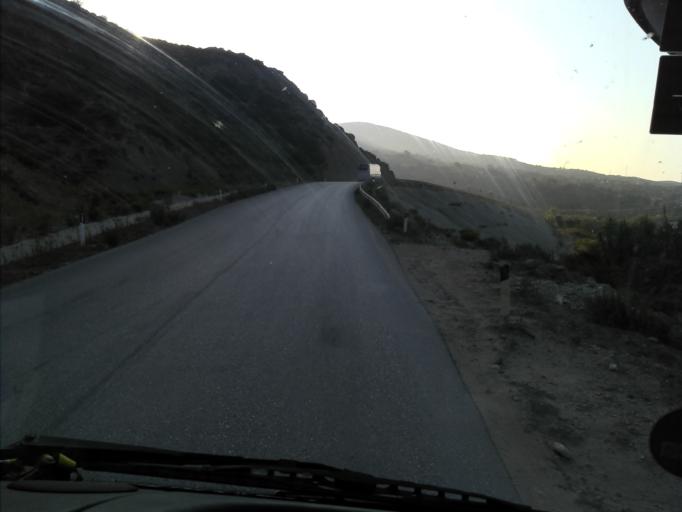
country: AL
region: Gjirokaster
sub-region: Rrethi i Tepelenes
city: Krahes
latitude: 40.3811
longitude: 19.9005
